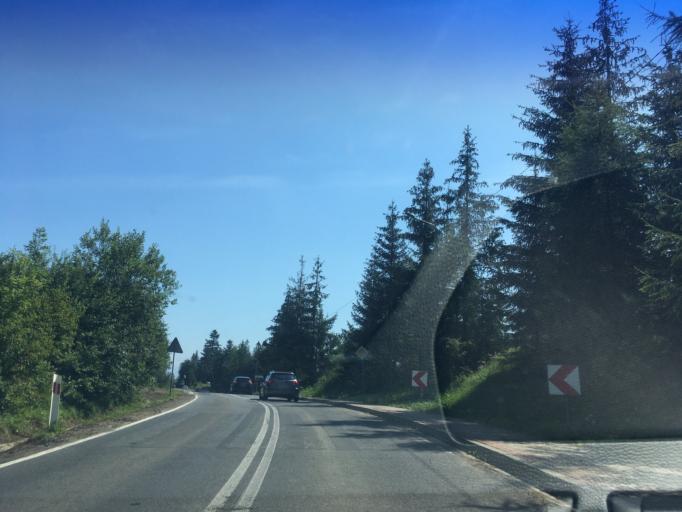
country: PL
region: Lesser Poland Voivodeship
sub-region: Powiat nowotarski
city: Maniowy
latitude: 49.4290
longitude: 20.2651
